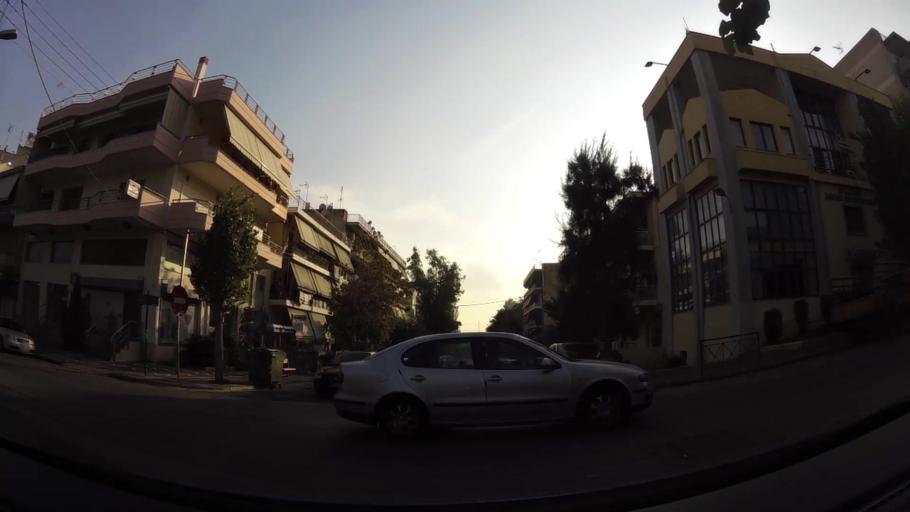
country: GR
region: Attica
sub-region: Nomarchia Athinas
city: Petroupolis
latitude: 38.0435
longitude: 23.6845
